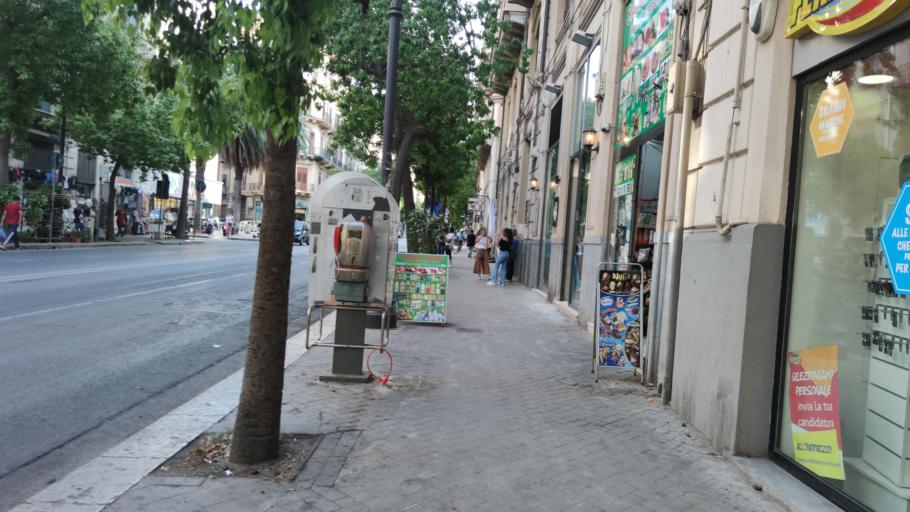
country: IT
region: Sicily
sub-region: Palermo
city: Palermo
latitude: 38.1135
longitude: 13.3651
